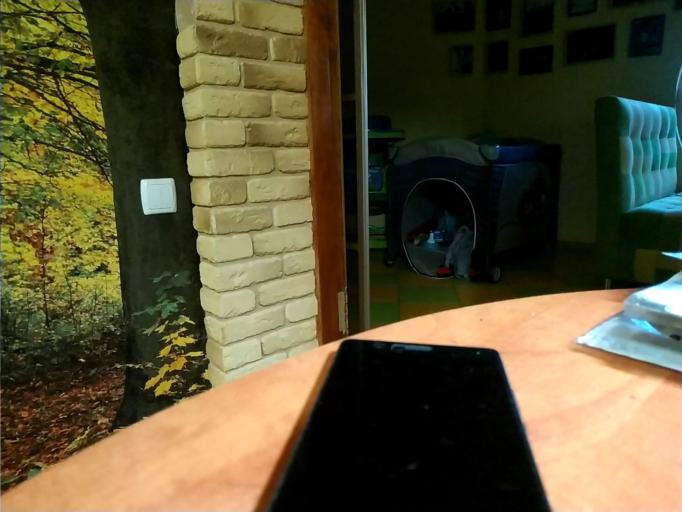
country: RU
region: Orjol
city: Znamenskoye
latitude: 53.4198
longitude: 35.5378
